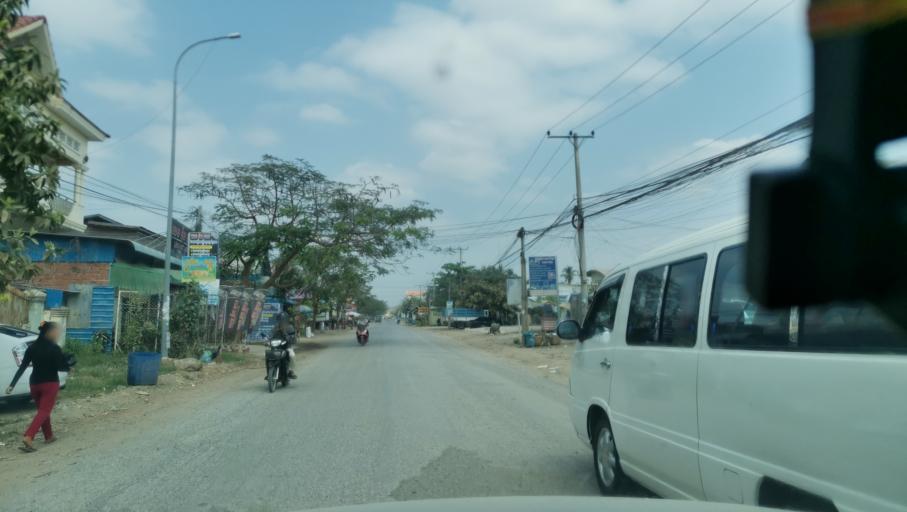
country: KH
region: Battambang
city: Battambang
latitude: 13.1095
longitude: 103.1958
